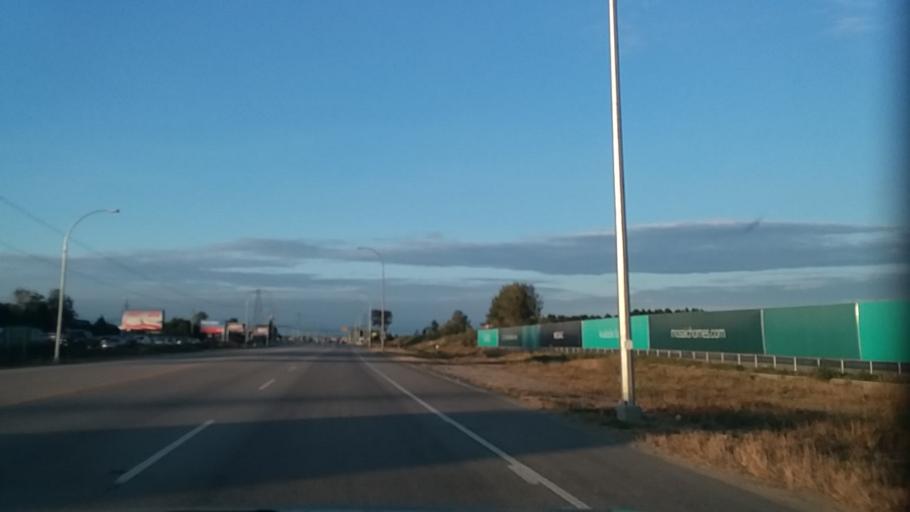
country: US
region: Washington
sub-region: Whatcom County
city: Point Roberts
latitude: 49.0301
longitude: -123.0951
